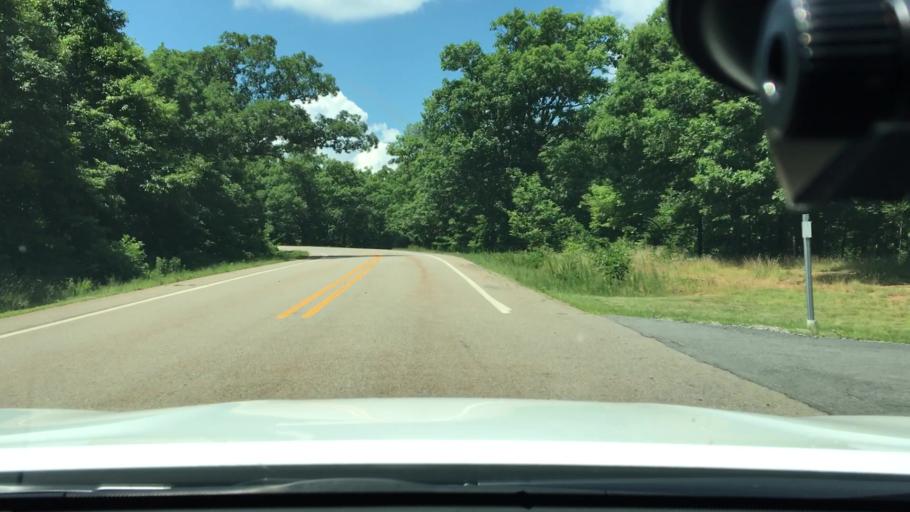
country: US
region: Arkansas
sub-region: Logan County
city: Paris
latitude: 35.1691
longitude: -93.6506
